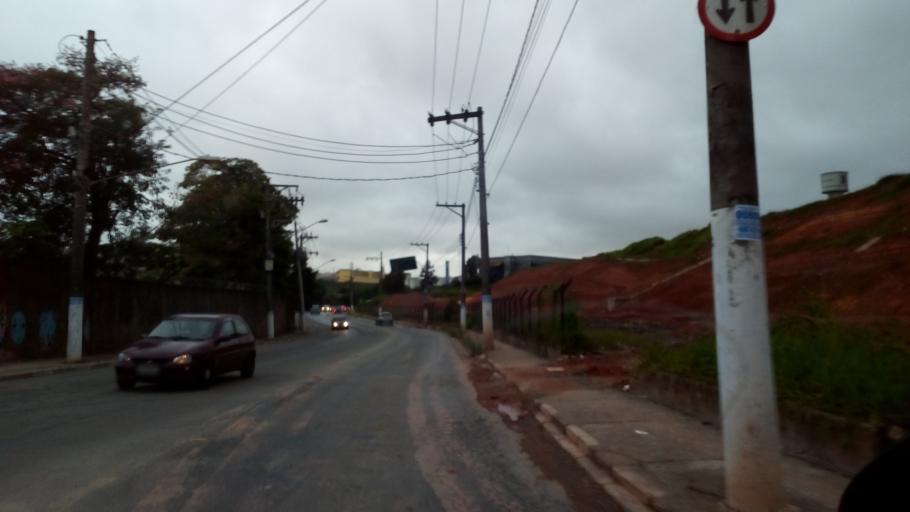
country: BR
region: Sao Paulo
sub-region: Itaquaquecetuba
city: Itaquaquecetuba
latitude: -23.4291
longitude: -46.4063
